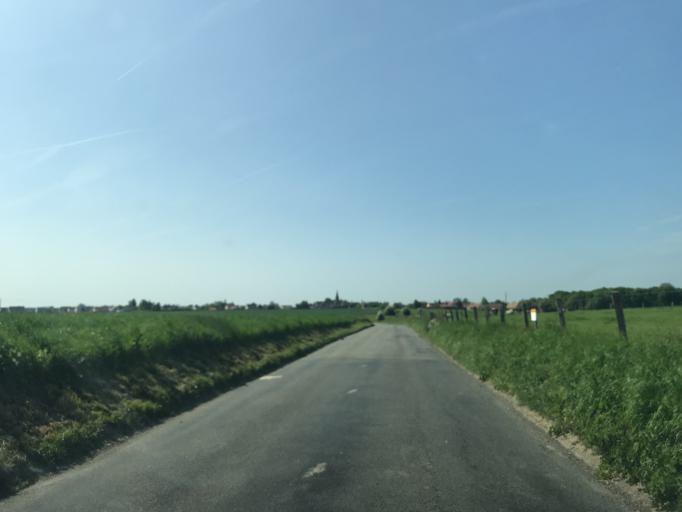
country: FR
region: Haute-Normandie
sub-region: Departement de la Seine-Maritime
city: Belbeuf
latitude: 49.3726
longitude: 1.1602
